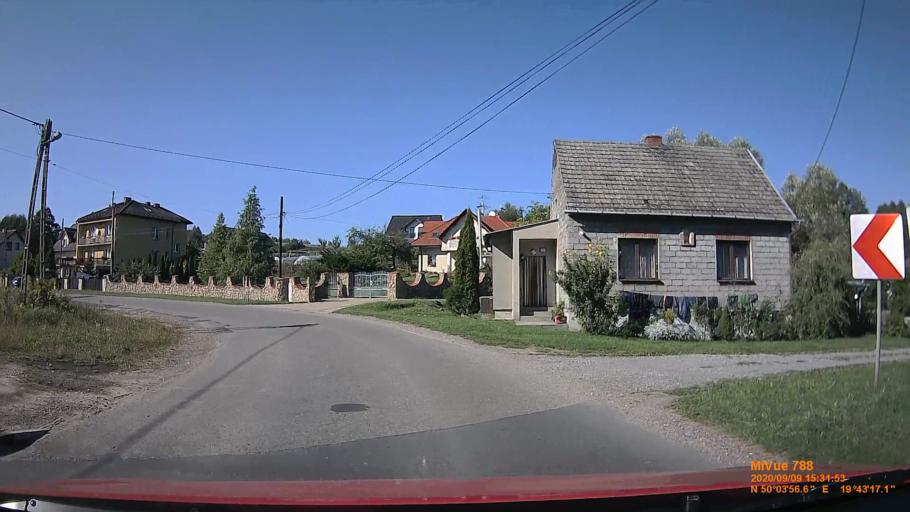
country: PL
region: Lesser Poland Voivodeship
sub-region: Powiat krakowski
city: Mnikow
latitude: 50.0657
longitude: 19.7214
